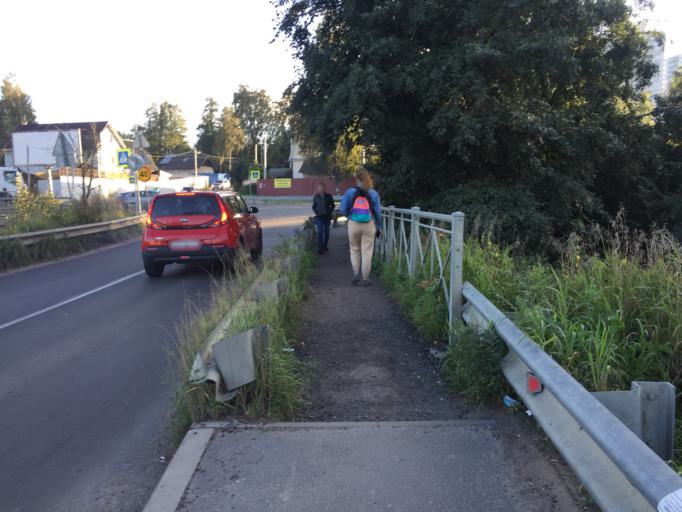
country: RU
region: Leningrad
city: Murino
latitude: 60.0540
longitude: 30.4563
